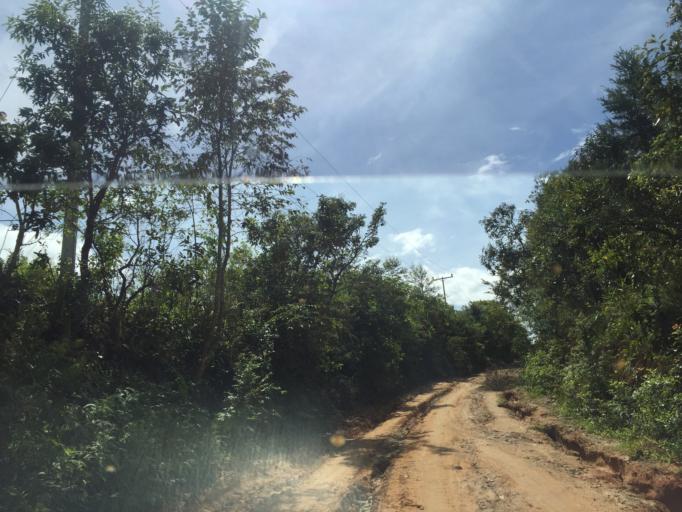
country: LA
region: Xiangkhoang
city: Muang Phonsavan
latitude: 19.3398
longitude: 103.5108
